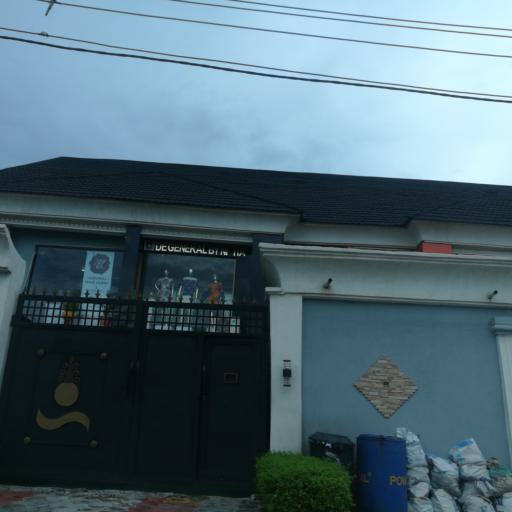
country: NG
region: Lagos
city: Ikoyi
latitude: 6.4415
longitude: 3.4786
